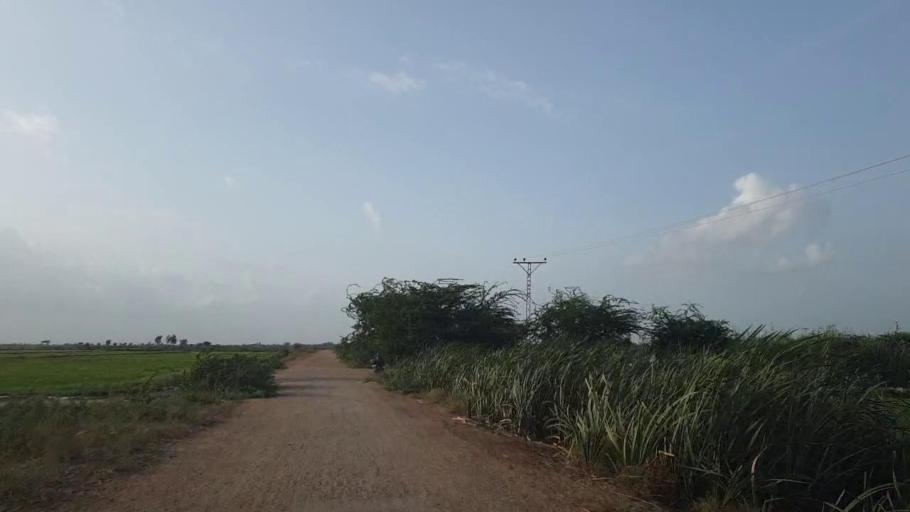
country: PK
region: Sindh
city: Tando Bago
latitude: 24.6593
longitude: 69.1120
